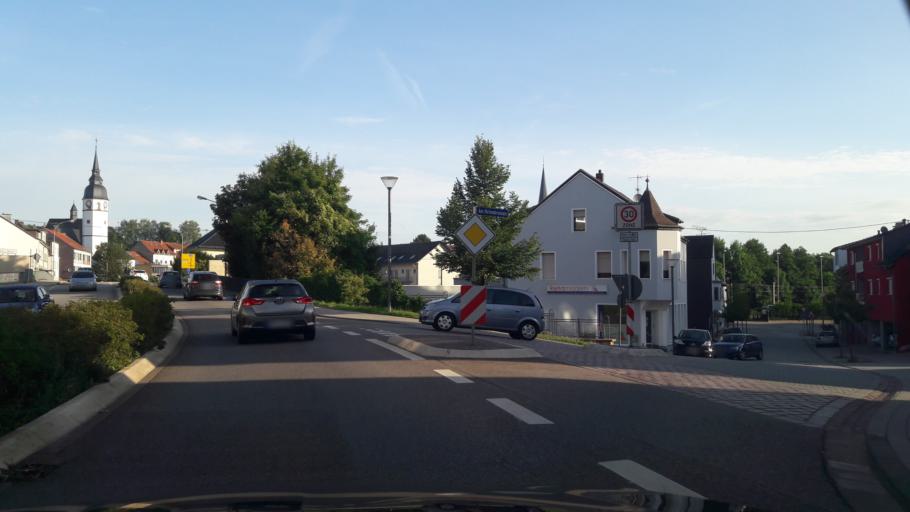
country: DE
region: Saarland
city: Heusweiler
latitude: 49.3361
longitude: 6.9306
